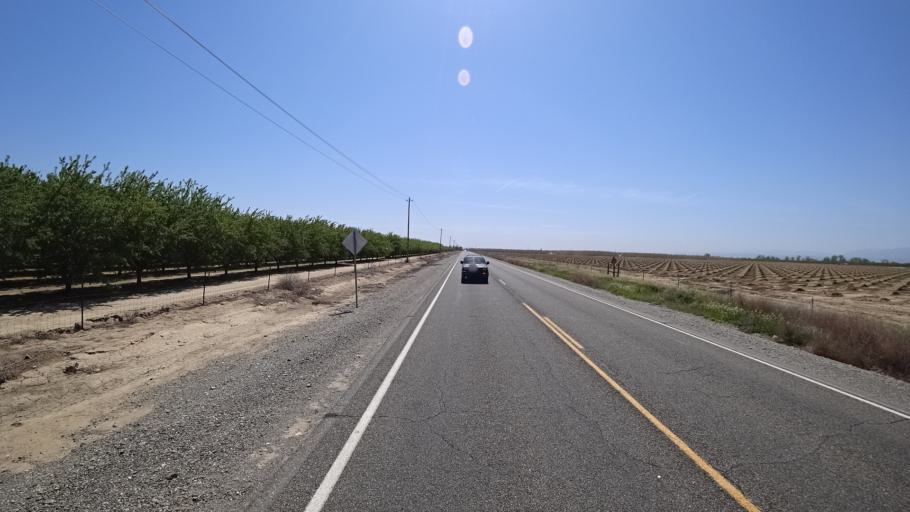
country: US
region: California
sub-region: Glenn County
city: Orland
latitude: 39.6520
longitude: -122.1971
